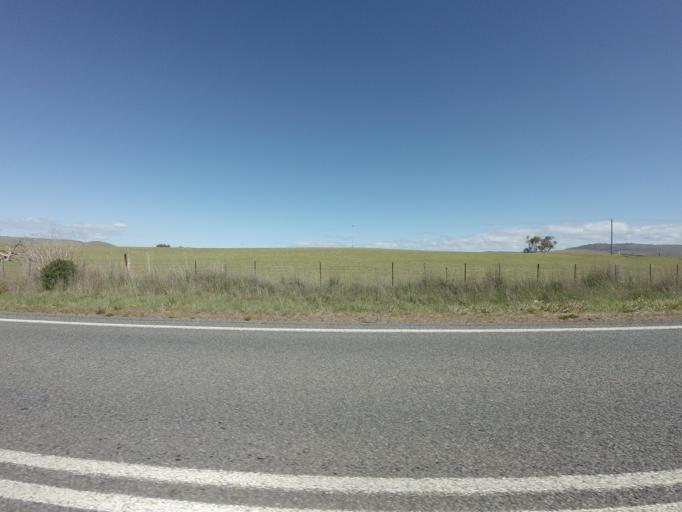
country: AU
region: Tasmania
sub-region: Derwent Valley
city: New Norfolk
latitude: -42.5531
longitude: 146.7987
